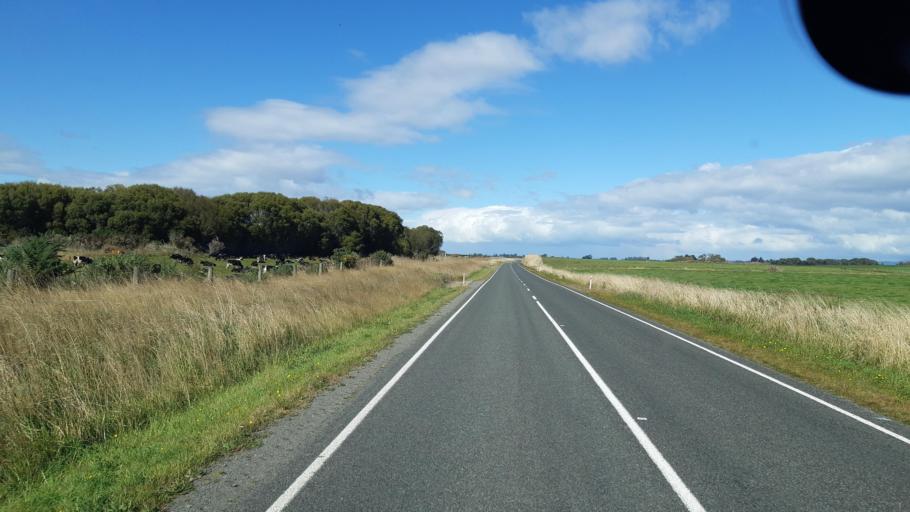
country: NZ
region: Southland
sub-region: Southland District
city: Winton
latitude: -45.9633
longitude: 168.1118
